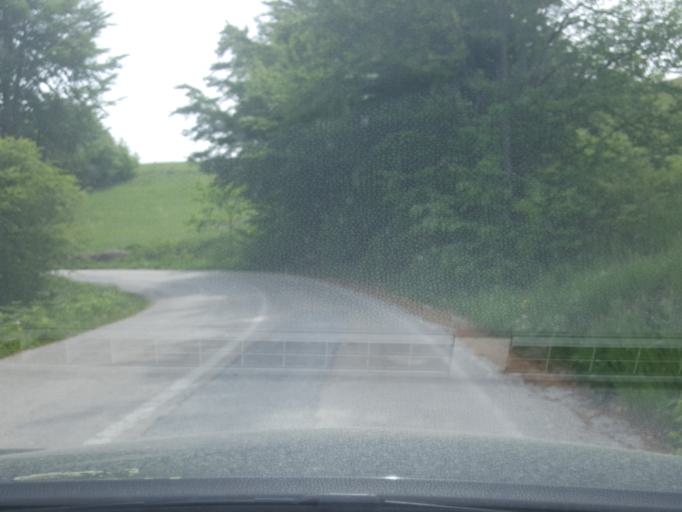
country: RS
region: Central Serbia
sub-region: Zlatiborski Okrug
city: Bajina Basta
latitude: 43.8958
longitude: 19.5200
